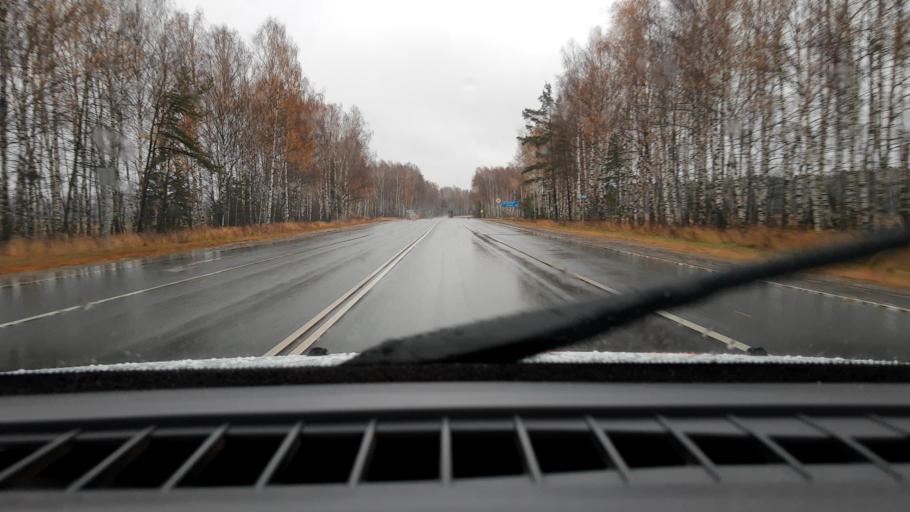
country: RU
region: Nizjnij Novgorod
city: Linda
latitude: 56.6536
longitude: 44.1194
